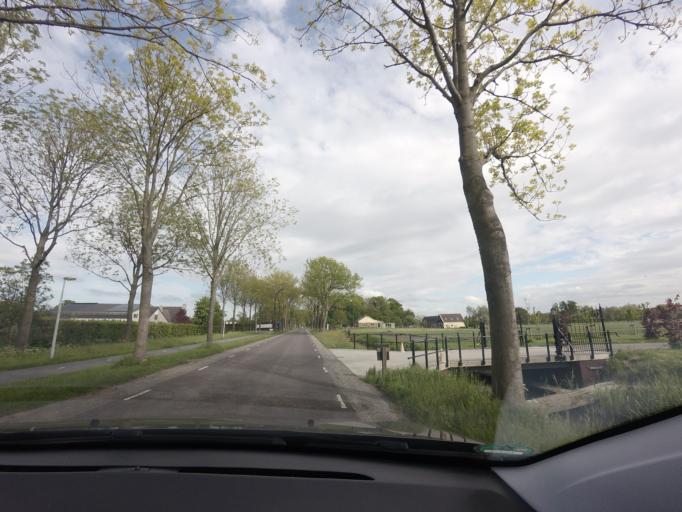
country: NL
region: North Holland
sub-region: Gemeente Beemster
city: Halfweg
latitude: 52.5215
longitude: 4.9074
